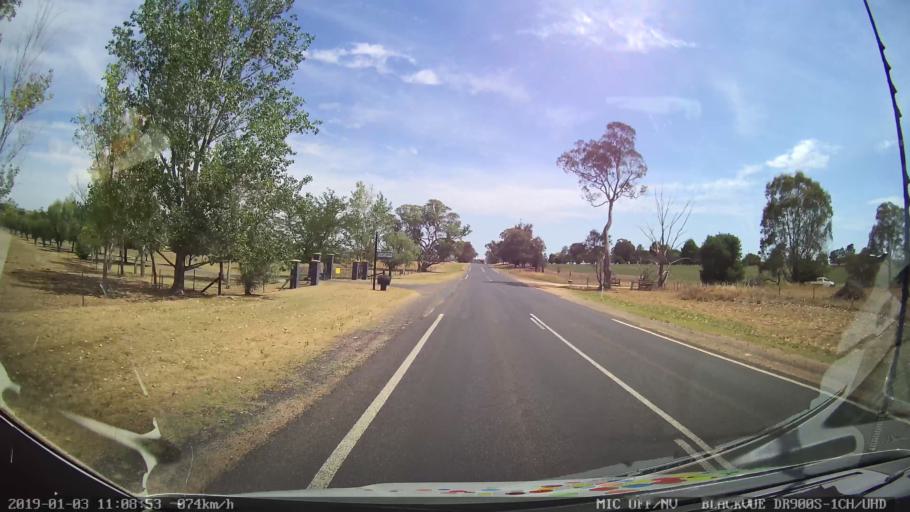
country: AU
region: New South Wales
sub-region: Young
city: Young
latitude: -34.2447
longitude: 148.2557
